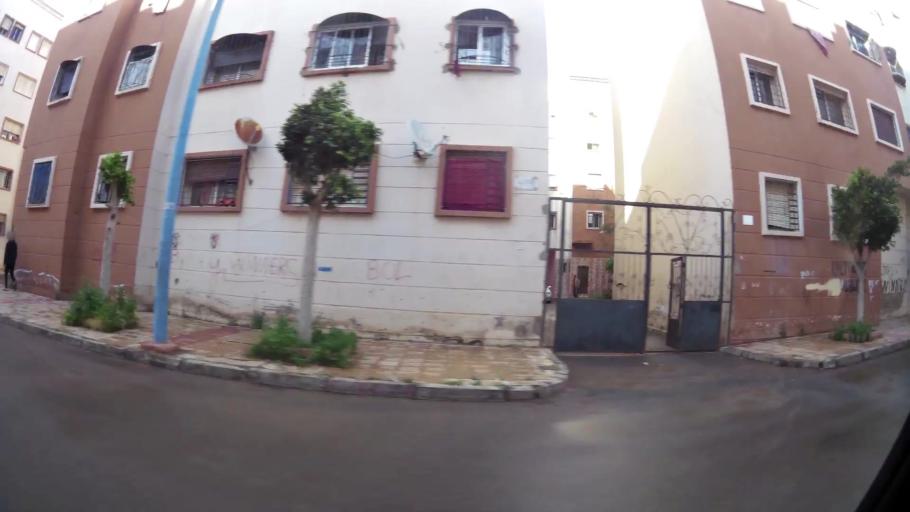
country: MA
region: Grand Casablanca
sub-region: Casablanca
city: Casablanca
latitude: 33.5555
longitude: -7.7051
